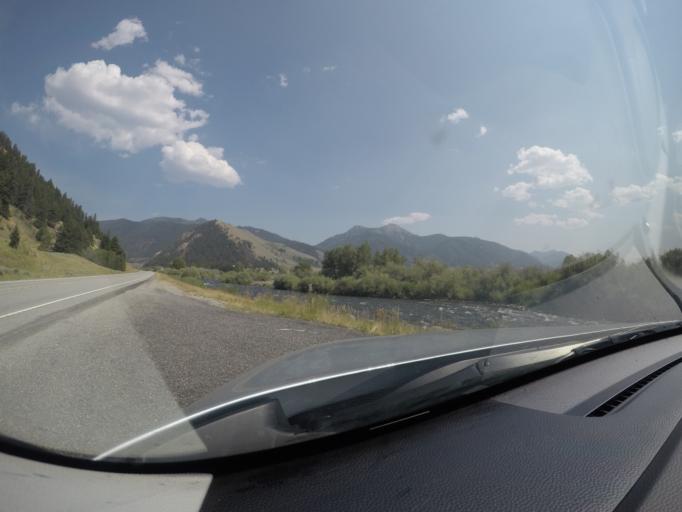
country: US
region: Montana
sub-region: Gallatin County
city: West Yellowstone
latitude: 44.8266
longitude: -111.4559
